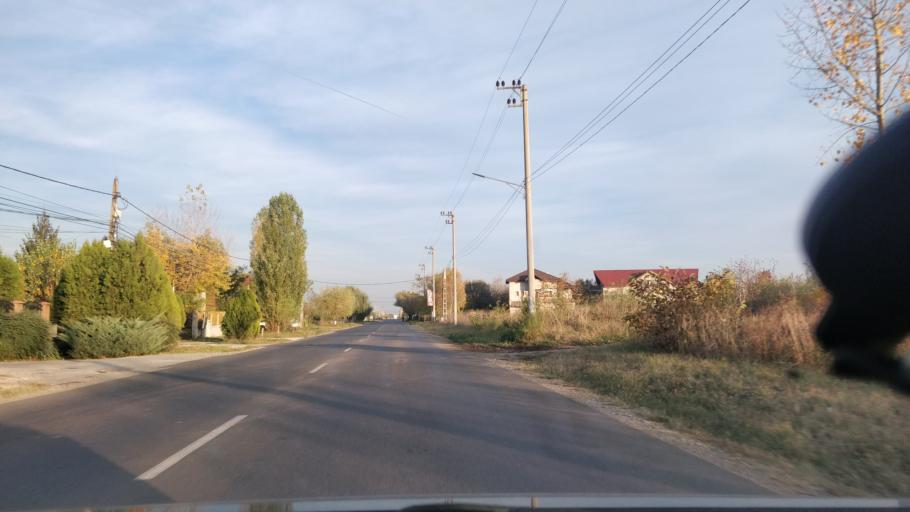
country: RO
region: Ilfov
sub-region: Comuna Ciorogarla
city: Ciorogarla
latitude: 44.4417
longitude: 25.9025
